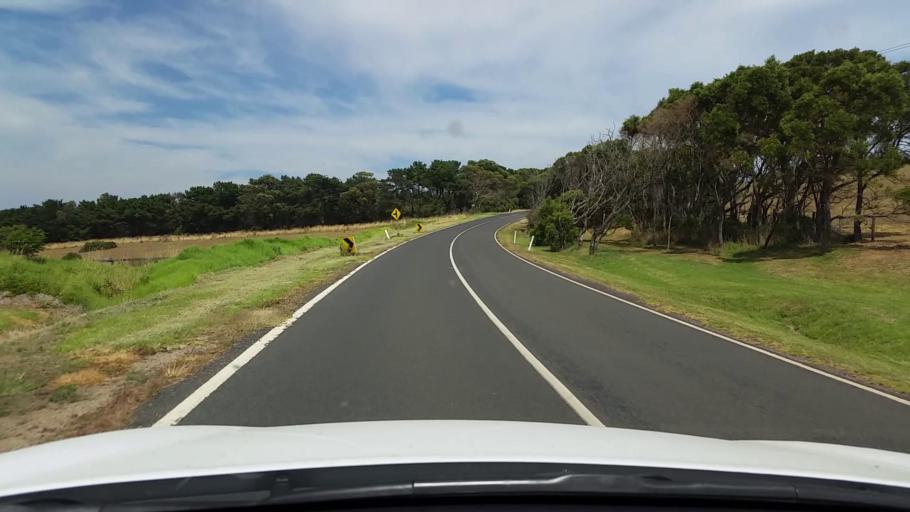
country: AU
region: Victoria
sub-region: Mornington Peninsula
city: Merricks
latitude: -38.4791
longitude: 144.9913
